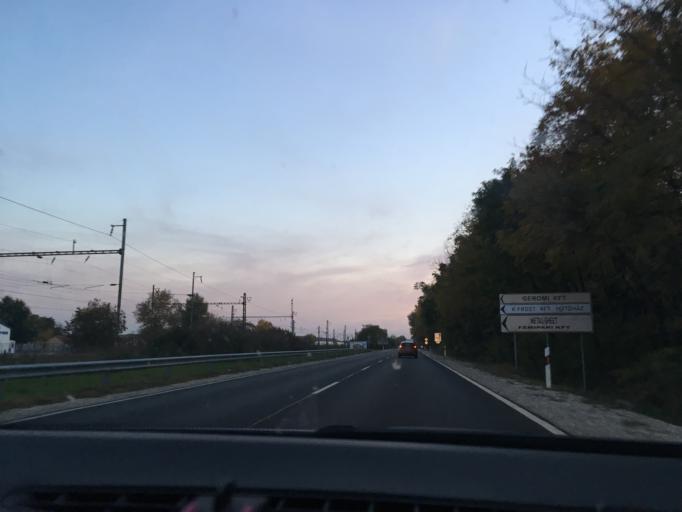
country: HU
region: Hajdu-Bihar
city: Debrecen
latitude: 47.5795
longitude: 21.6545
